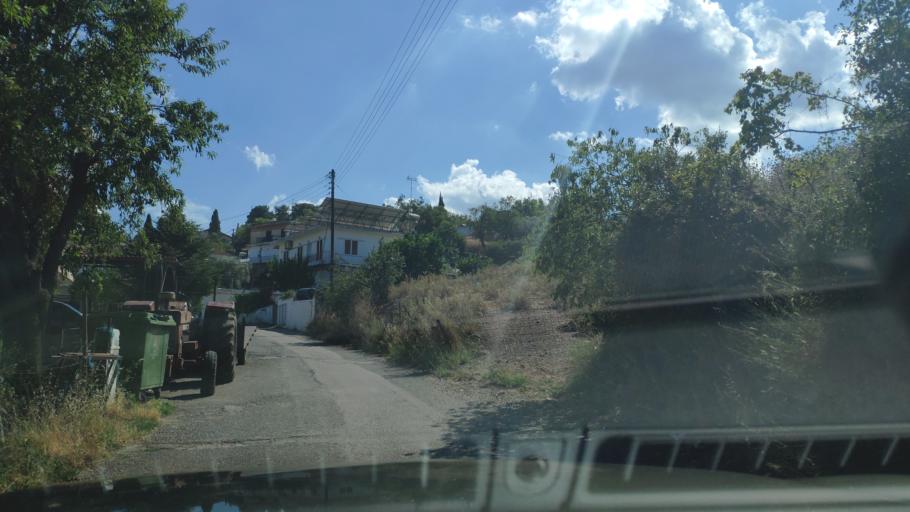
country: GR
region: West Greece
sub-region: Nomos Aitolias kai Akarnanias
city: Katouna
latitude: 38.7899
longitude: 21.1153
